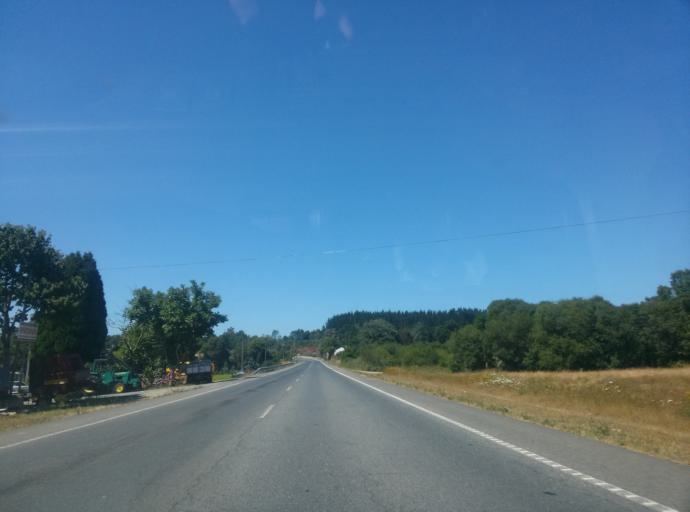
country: ES
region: Galicia
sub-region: Provincia de Lugo
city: Mos
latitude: 43.1217
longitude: -7.4857
